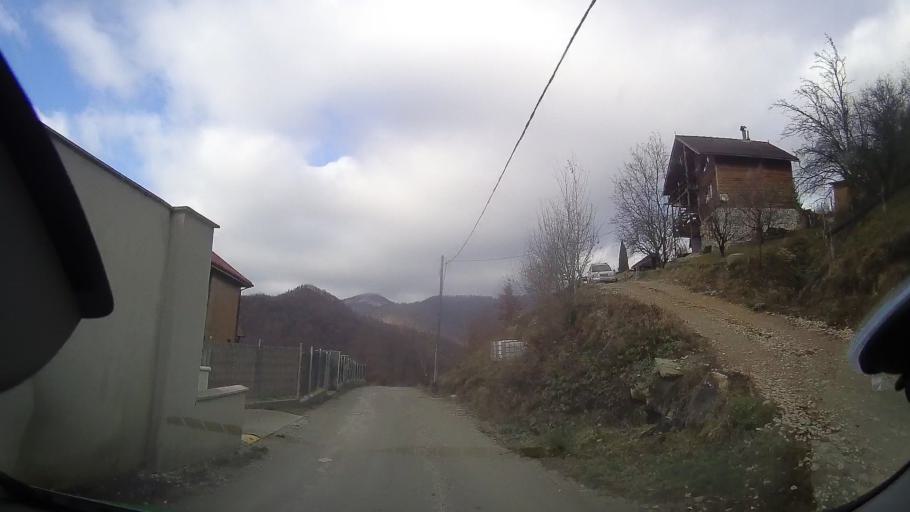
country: RO
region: Cluj
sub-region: Comuna Valea Ierii
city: Valea Ierii
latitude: 46.6785
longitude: 23.3101
